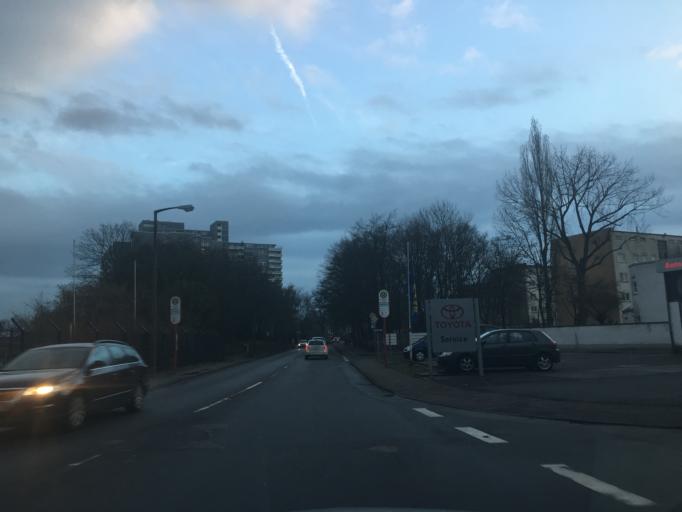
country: DE
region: Hesse
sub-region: Regierungsbezirk Darmstadt
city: Hattersheim
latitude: 50.0744
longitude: 8.5005
